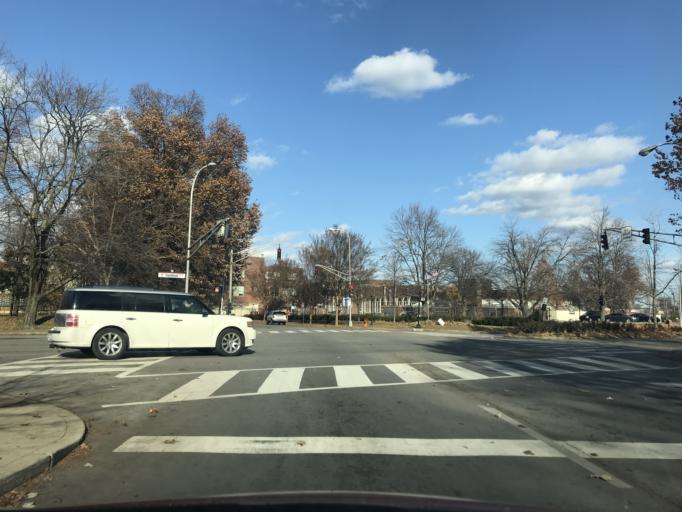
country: US
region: Kentucky
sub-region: Jefferson County
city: Louisville
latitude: 38.2202
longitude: -85.7600
